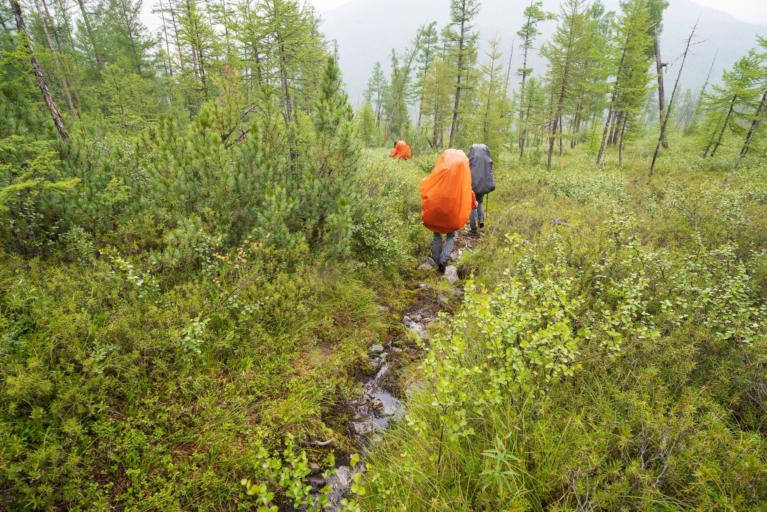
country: RU
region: Transbaikal Territory
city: Kuanda
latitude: 56.4946
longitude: 116.3955
